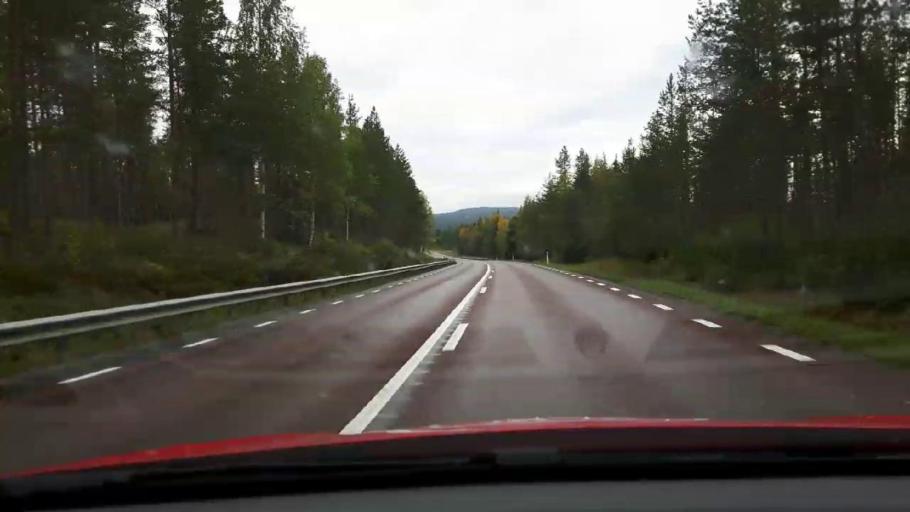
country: SE
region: Jaemtland
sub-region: Bergs Kommun
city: Hoverberg
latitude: 62.8236
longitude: 14.5164
